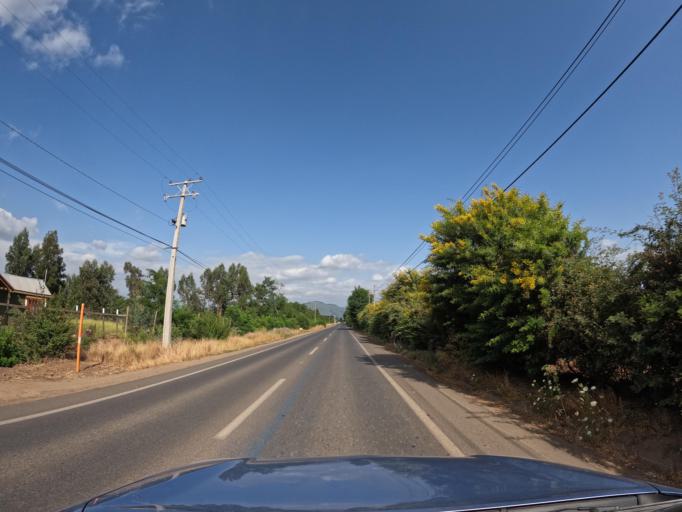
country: CL
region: Maule
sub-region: Provincia de Curico
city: Molina
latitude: -35.2780
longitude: -71.2775
